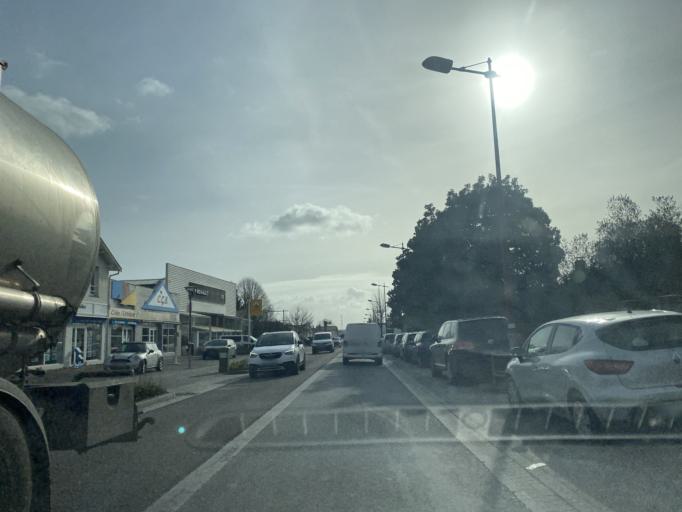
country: FR
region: Aquitaine
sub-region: Departement de la Gironde
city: Le Taillan-Medoc
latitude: 44.9088
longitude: -0.6690
